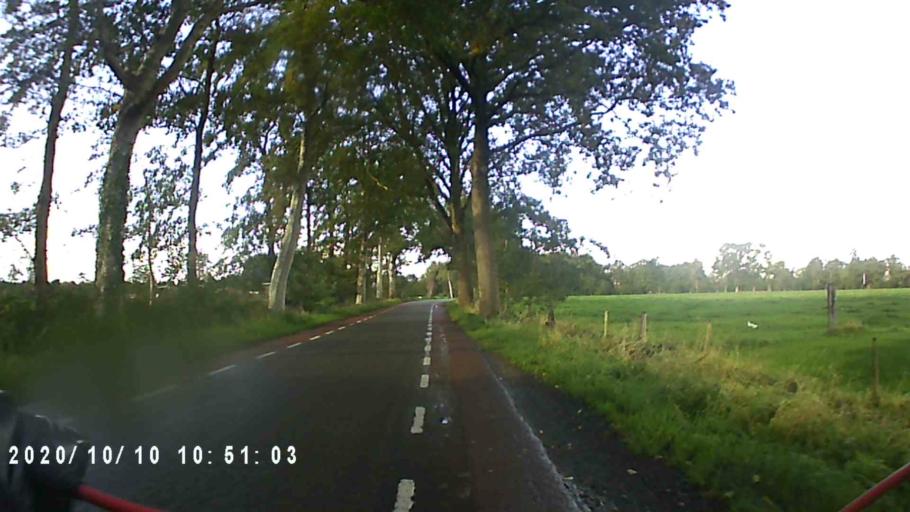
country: NL
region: Friesland
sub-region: Gemeente Achtkarspelen
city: Surhuisterveen
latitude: 53.1595
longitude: 6.2311
